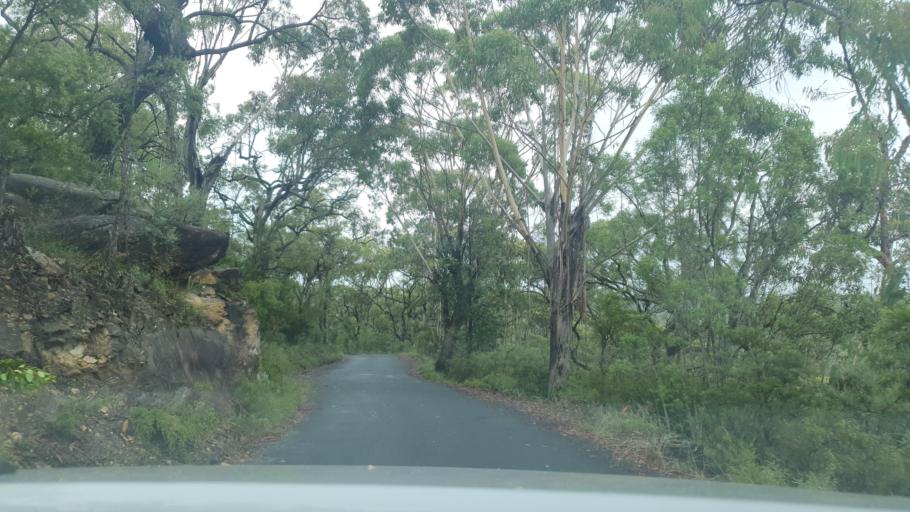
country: AU
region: New South Wales
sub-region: Blue Mountains Municipality
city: Glenbrook
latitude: -33.7784
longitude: 150.6195
